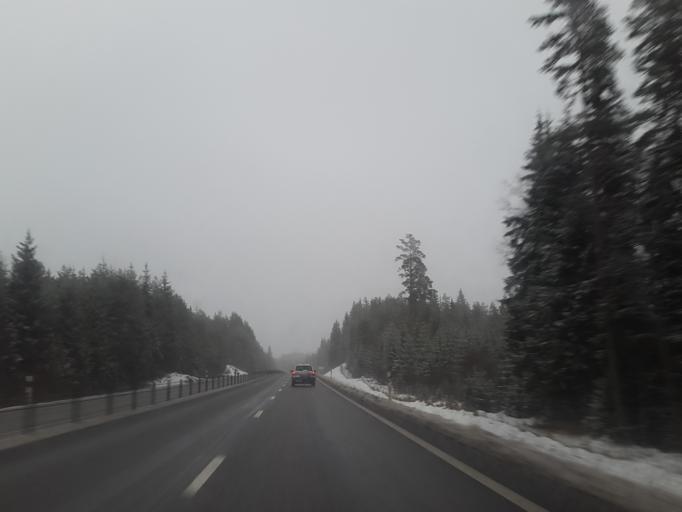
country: SE
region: Joenkoeping
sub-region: Mullsjo Kommun
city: Mullsjoe
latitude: 57.7660
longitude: 13.7683
